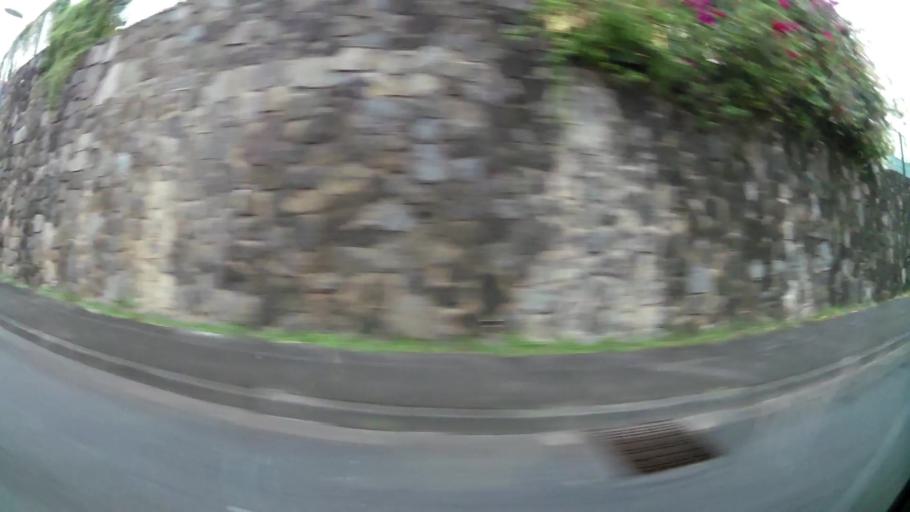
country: RE
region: Reunion
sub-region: Reunion
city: Saint-Denis
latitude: -20.9003
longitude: 55.4674
